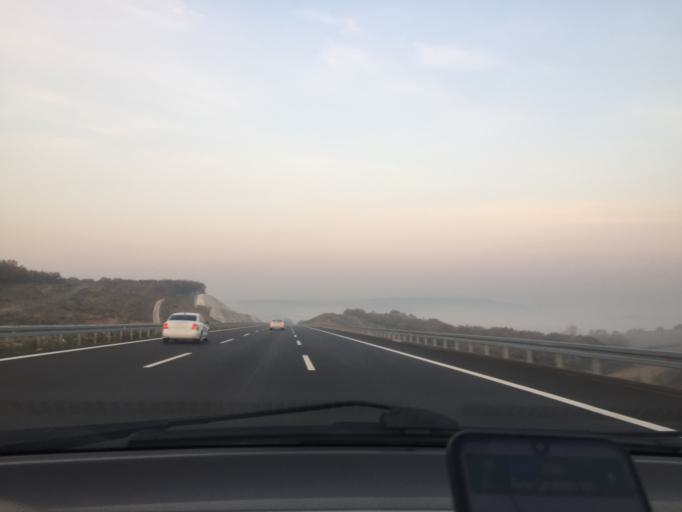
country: TR
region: Bursa
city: Mahmudiye
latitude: 40.2599
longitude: 28.6824
